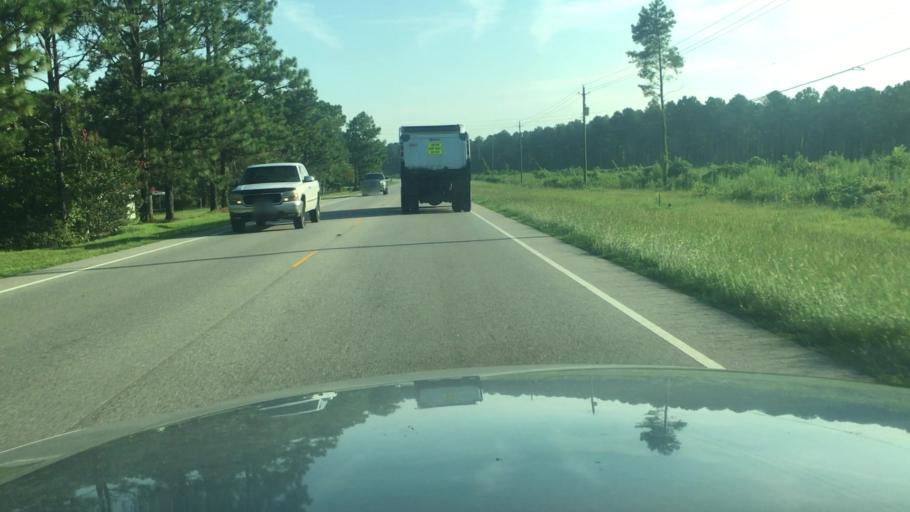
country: US
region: North Carolina
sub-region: Harnett County
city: Walkertown
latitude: 35.1907
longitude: -78.8508
